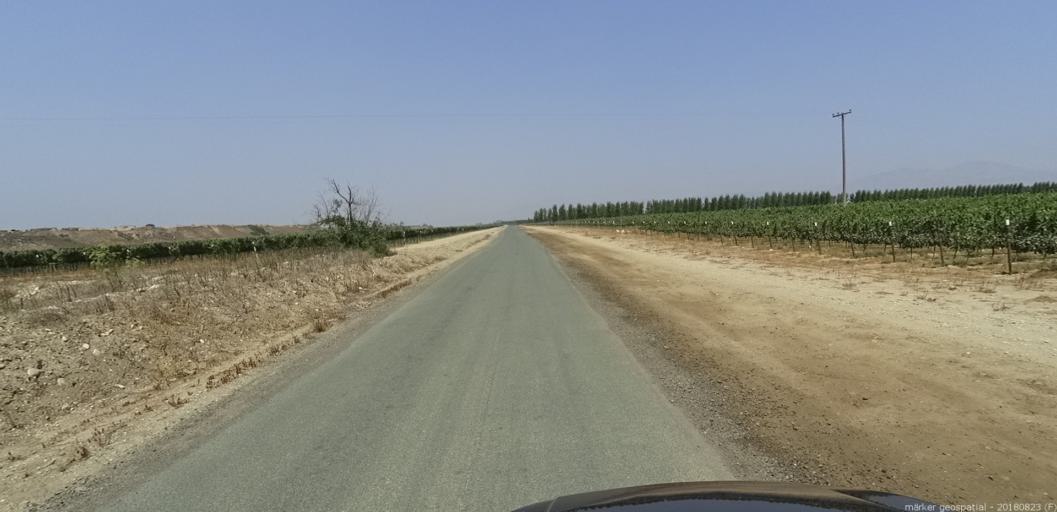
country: US
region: California
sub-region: Monterey County
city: Greenfield
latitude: 36.3311
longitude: -121.2963
